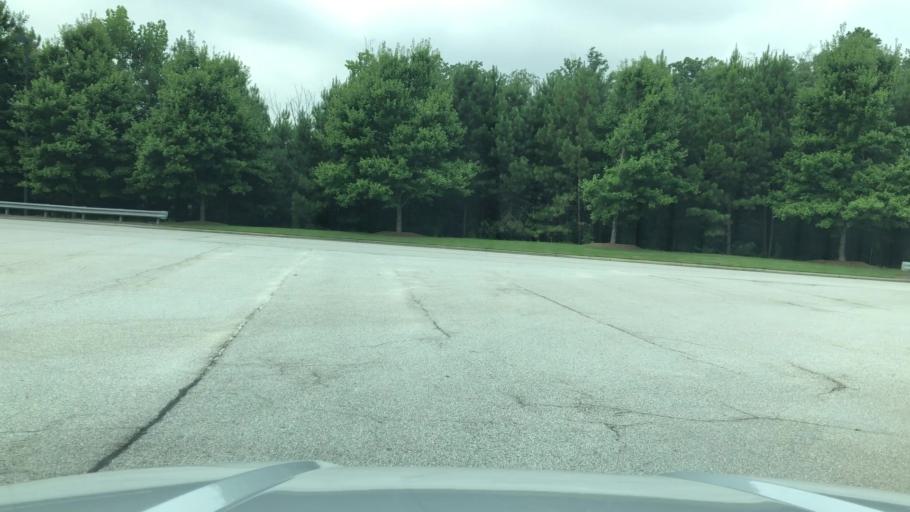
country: US
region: Georgia
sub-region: Cobb County
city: Mableton
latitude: 33.7693
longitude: -84.5747
